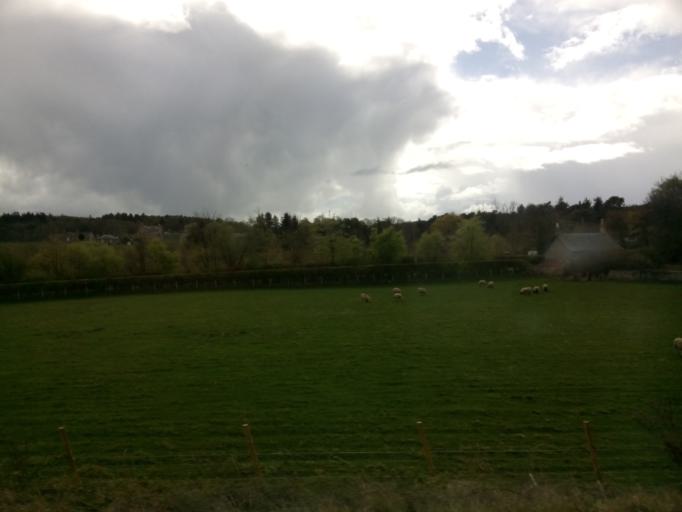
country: GB
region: Scotland
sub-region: East Lothian
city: Dunbar
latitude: 55.9455
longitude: -2.3788
